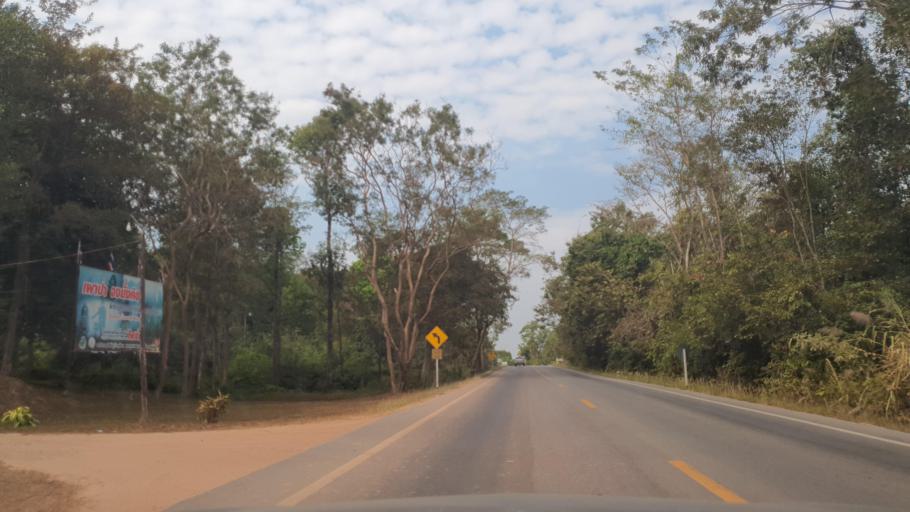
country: TH
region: Changwat Bueng Kan
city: Bung Khla
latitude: 18.2888
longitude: 103.8922
